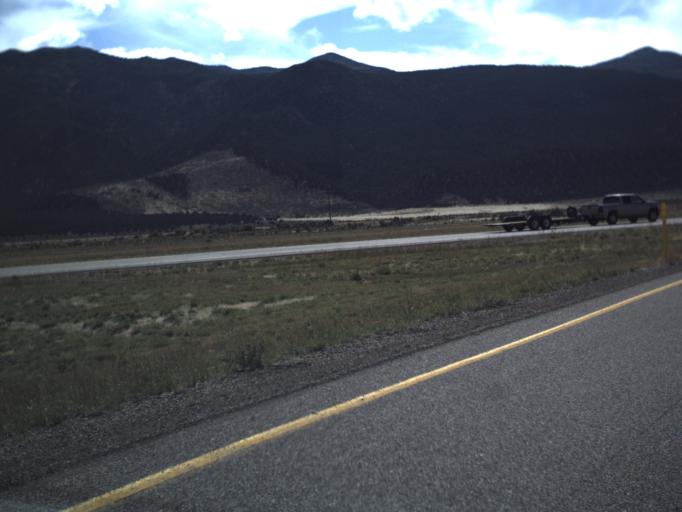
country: US
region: Utah
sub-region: Iron County
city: Enoch
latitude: 37.8017
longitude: -112.9492
